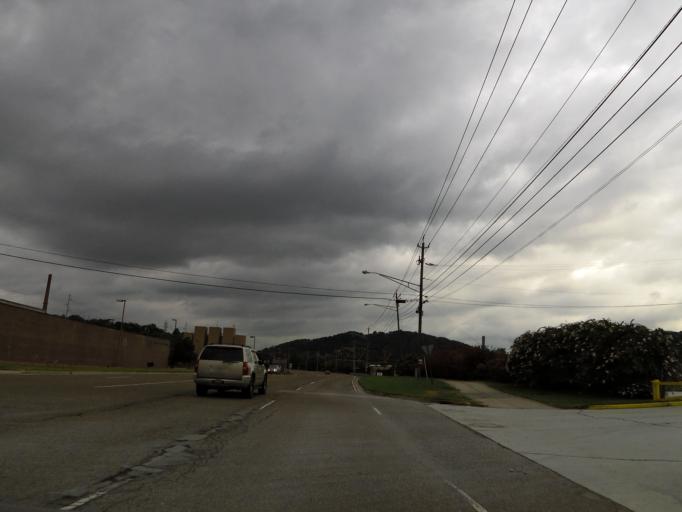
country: US
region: Tennessee
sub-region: Knox County
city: Knoxville
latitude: 35.9441
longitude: -83.9302
